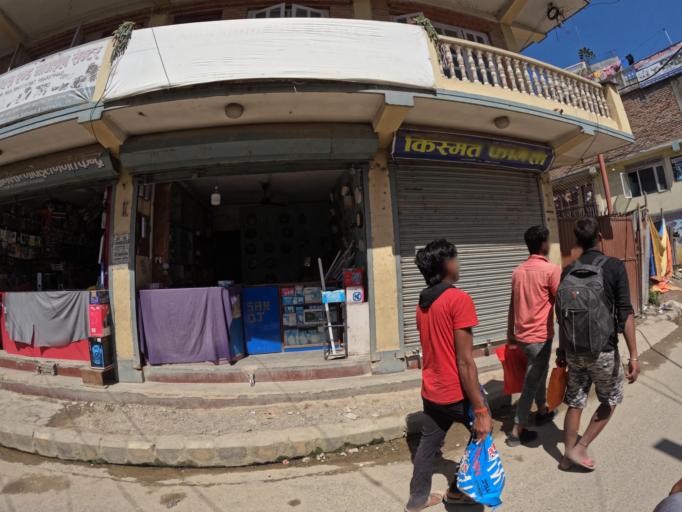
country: NP
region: Central Region
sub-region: Bagmati Zone
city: Kathmandu
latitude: 27.7436
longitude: 85.3300
